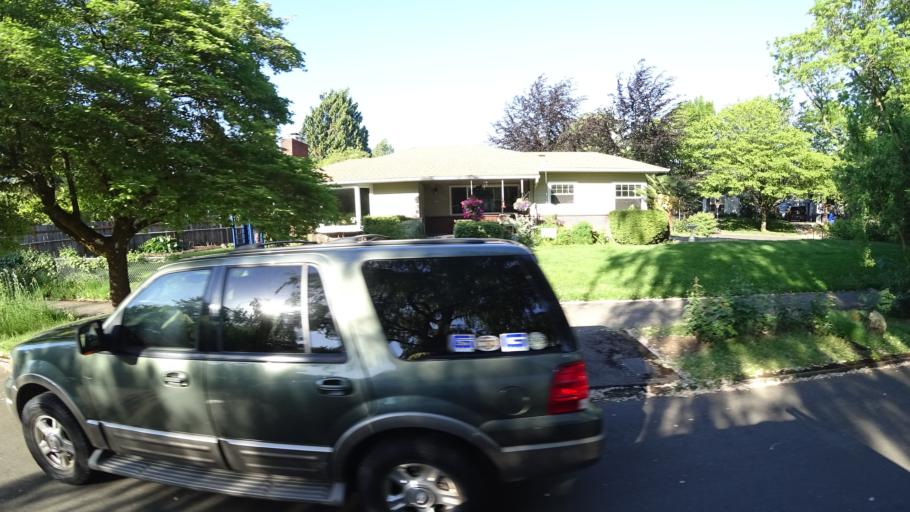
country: US
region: Oregon
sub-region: Multnomah County
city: Portland
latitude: 45.5529
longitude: -122.6875
